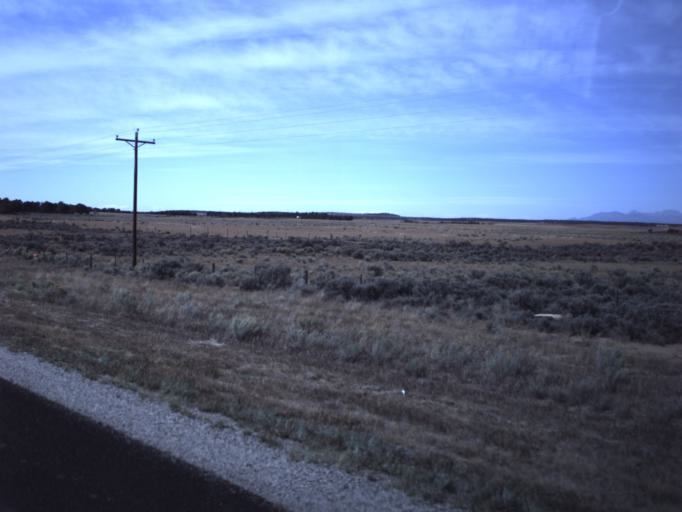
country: US
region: Colorado
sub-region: Dolores County
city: Dove Creek
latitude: 37.8205
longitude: -109.0560
